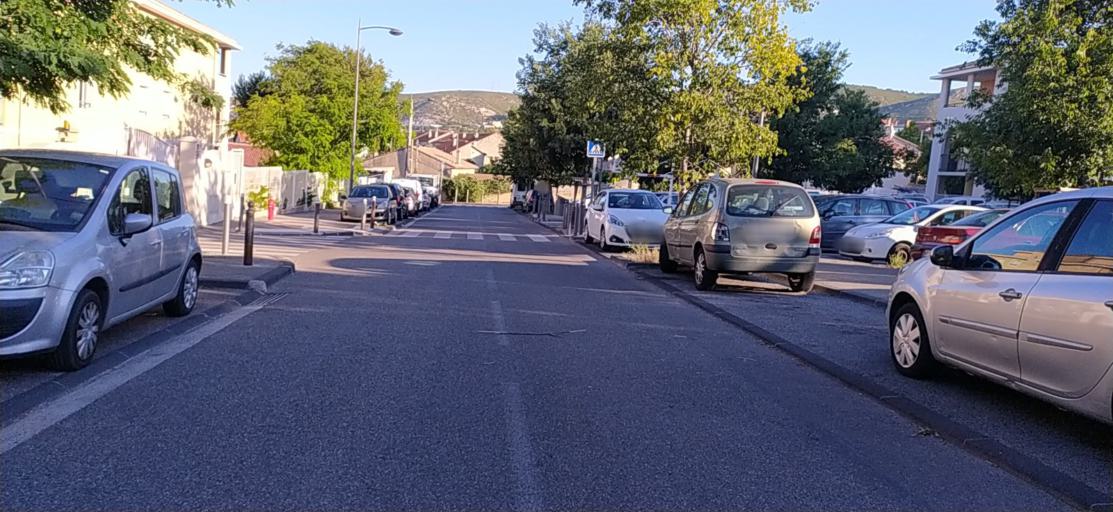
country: FR
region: Provence-Alpes-Cote d'Azur
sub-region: Departement des Bouches-du-Rhone
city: Marseille 16
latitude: 43.3563
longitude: 5.3413
